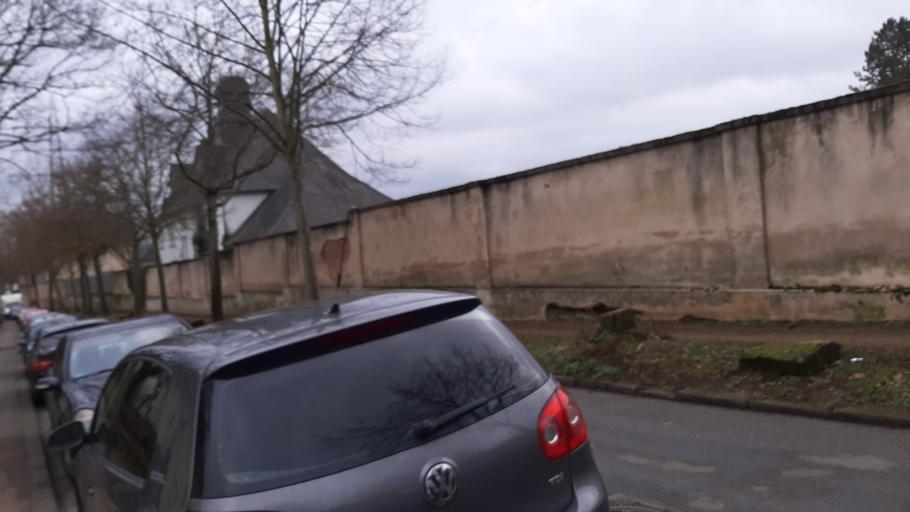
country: DE
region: Rheinland-Pfalz
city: Trier
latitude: 49.7503
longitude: 6.6158
